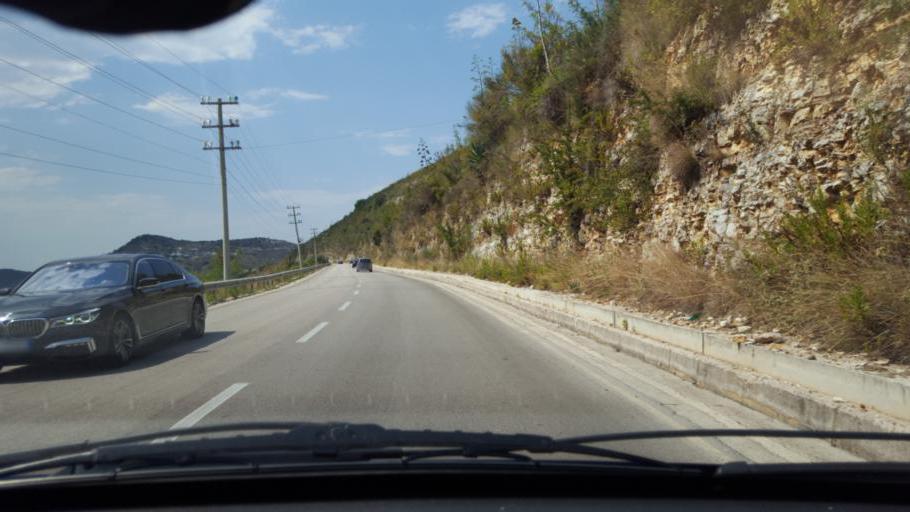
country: AL
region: Vlore
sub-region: Rrethi i Sarandes
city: Sarande
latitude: 39.8180
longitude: 20.0167
